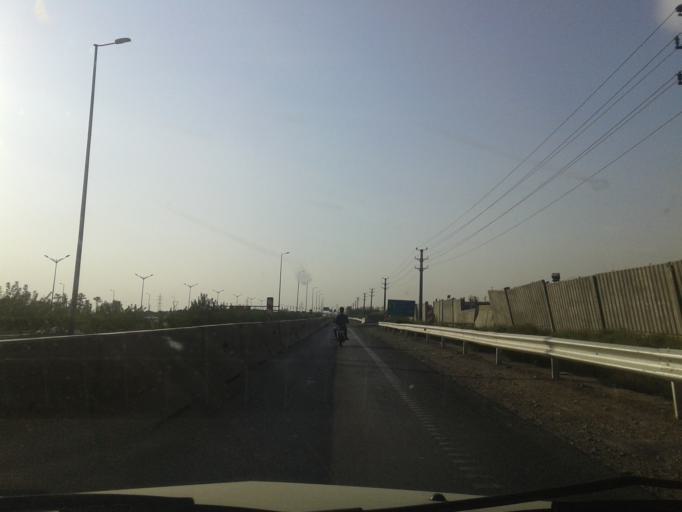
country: IR
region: Tehran
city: Eslamshahr
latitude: 35.6571
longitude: 51.2565
